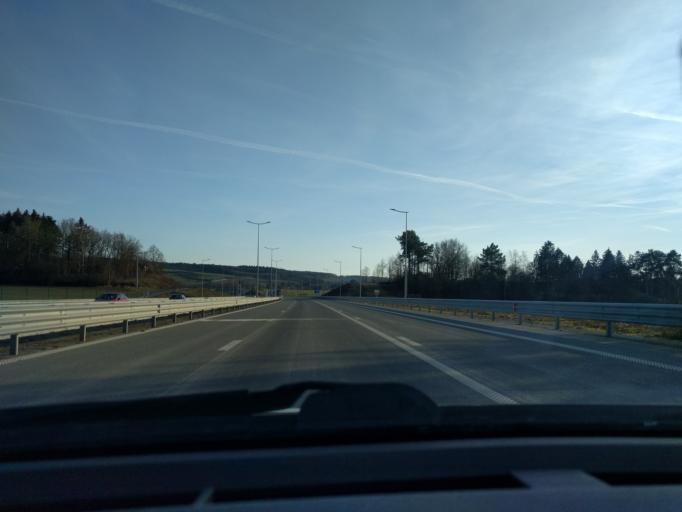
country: BE
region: Wallonia
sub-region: Province de Namur
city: Couvin
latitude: 50.0599
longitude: 4.5056
